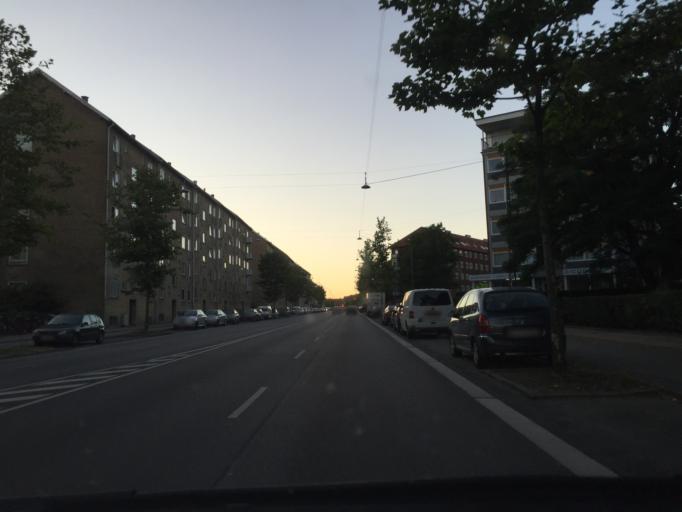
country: DK
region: Capital Region
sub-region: Frederiksberg Kommune
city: Frederiksberg
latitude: 55.7108
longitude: 12.5375
